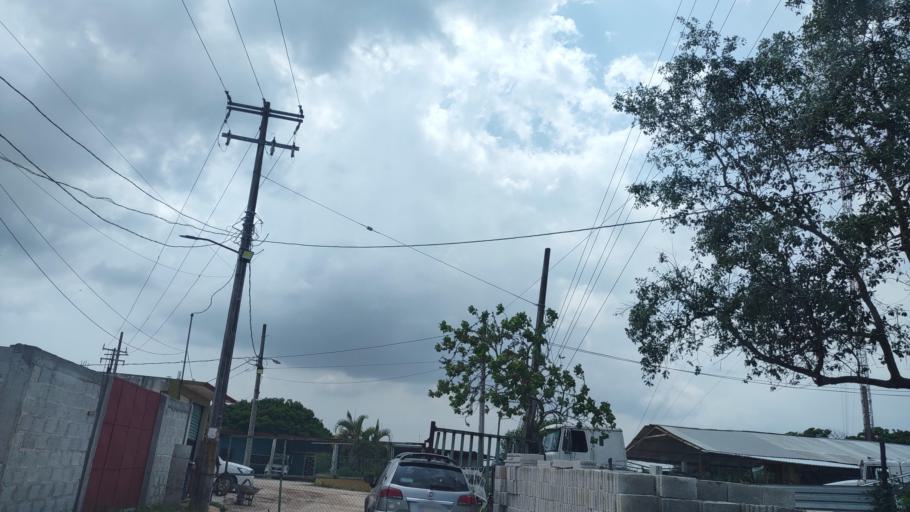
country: MX
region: Veracruz
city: Las Choapas
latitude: 17.9081
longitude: -94.1155
